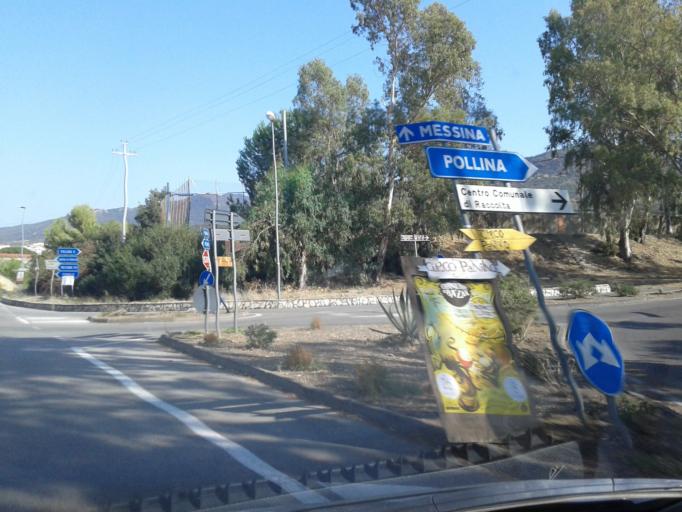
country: IT
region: Sicily
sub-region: Palermo
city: Finale
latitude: 38.0230
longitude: 14.1531
